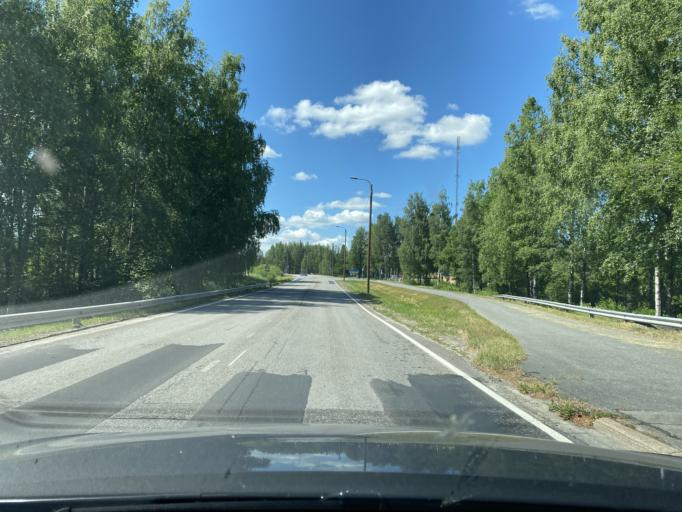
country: FI
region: Satakunta
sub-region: Rauma
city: Eura
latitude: 61.1158
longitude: 22.1504
